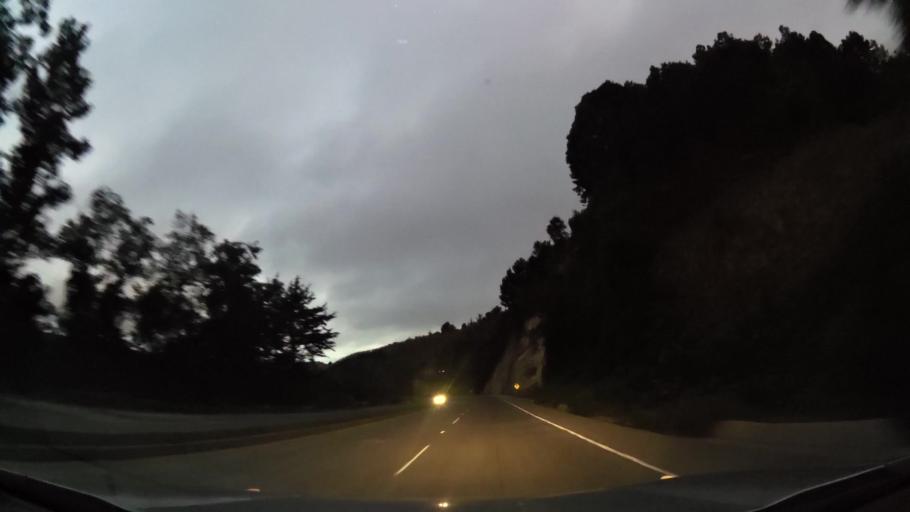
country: GT
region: Chimaltenango
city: Santa Apolonia
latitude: 14.8159
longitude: -90.9971
